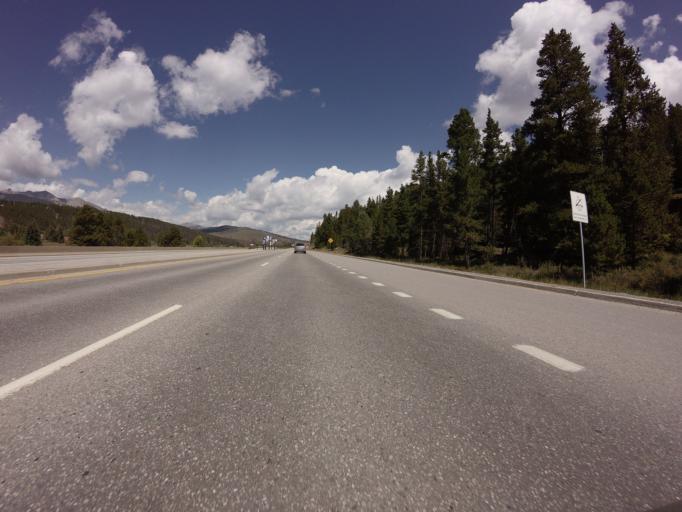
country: US
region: Colorado
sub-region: Summit County
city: Breckenridge
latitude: 39.4990
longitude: -106.0465
